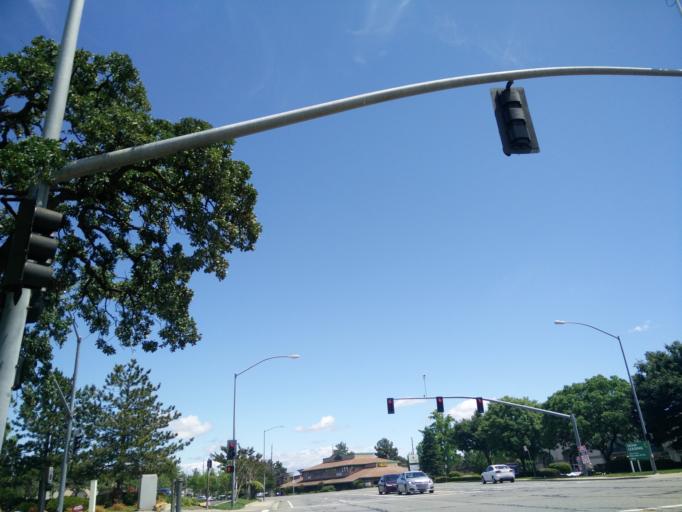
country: US
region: California
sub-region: Shasta County
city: Redding
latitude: 40.5862
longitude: -122.3563
